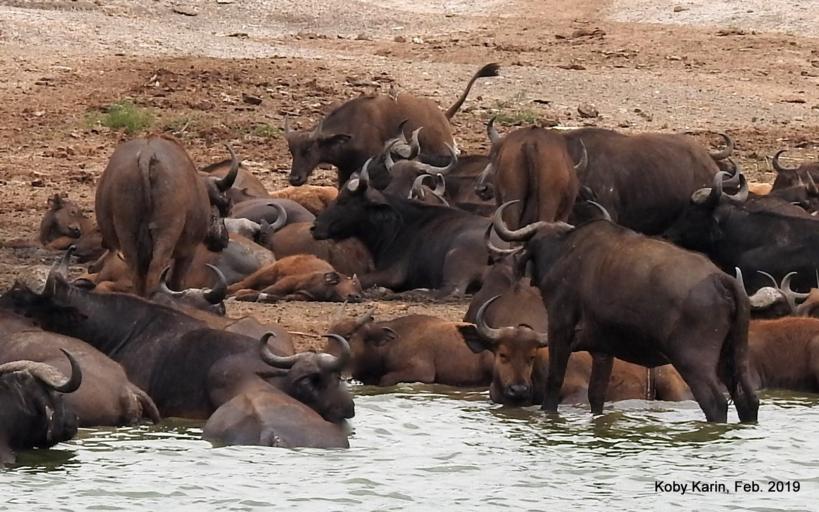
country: UG
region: Western Region
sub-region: Rubirizi District
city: Rubirizi
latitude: -0.1878
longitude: 29.9070
